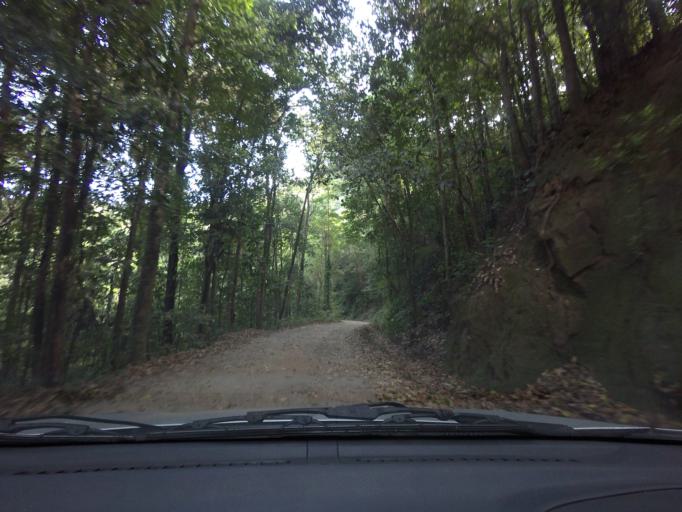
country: IN
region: Karnataka
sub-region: Kodagu
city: Somvarpet
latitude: 12.7206
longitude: 75.6628
